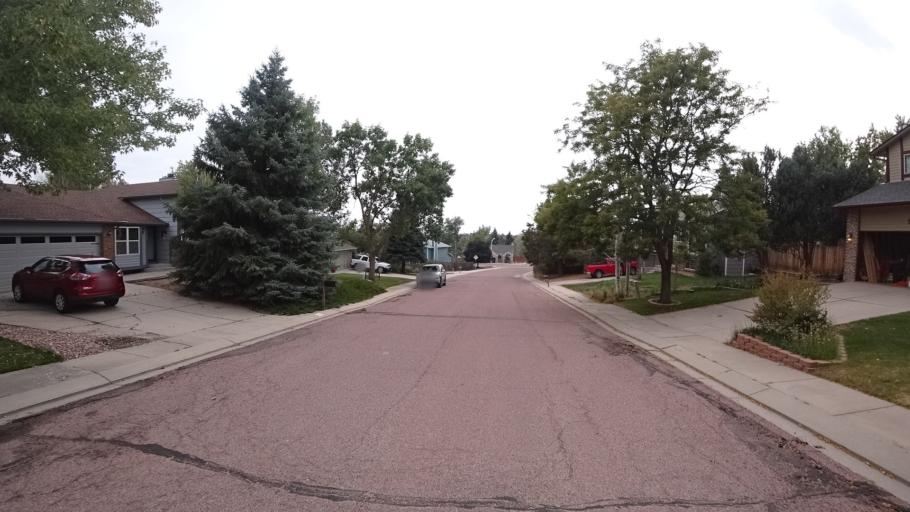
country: US
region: Colorado
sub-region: El Paso County
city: Cimarron Hills
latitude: 38.9079
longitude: -104.7275
